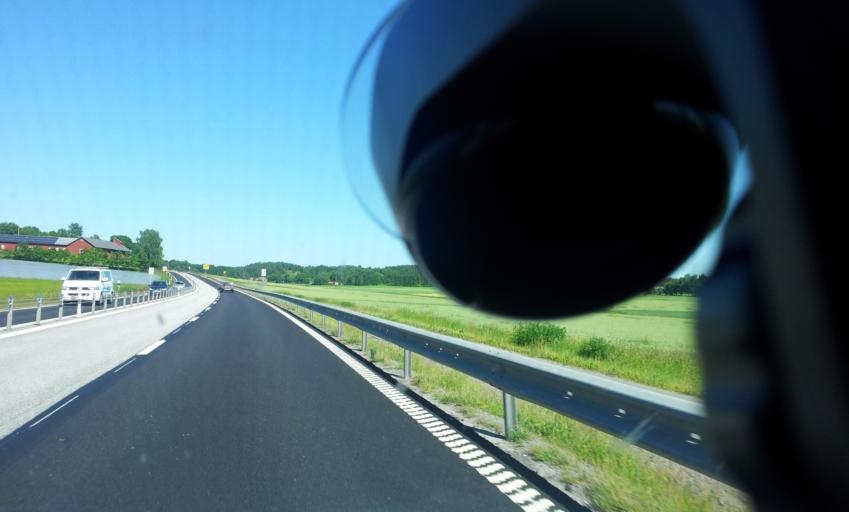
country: SE
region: OEstergoetland
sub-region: Soderkopings Kommun
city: Soederkoeping
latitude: 58.5369
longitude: 16.2813
